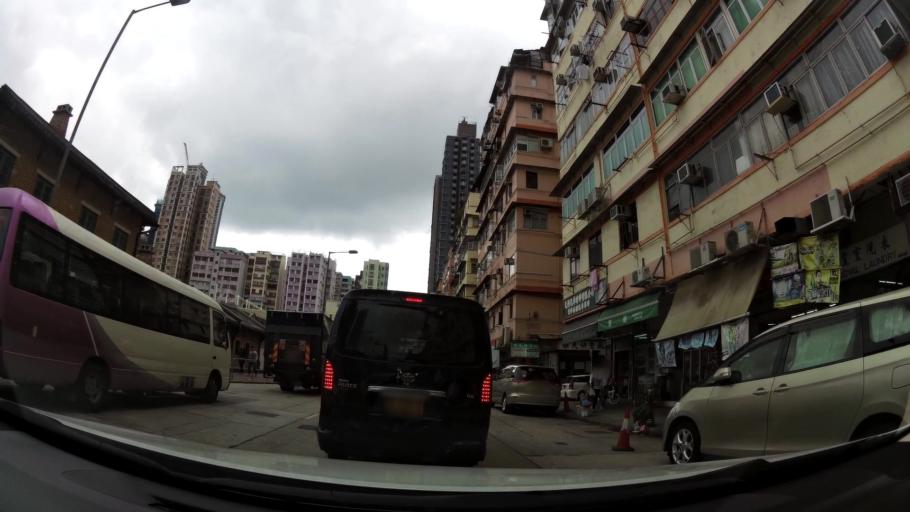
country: HK
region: Kowloon City
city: Kowloon
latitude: 22.3211
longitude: 114.1918
